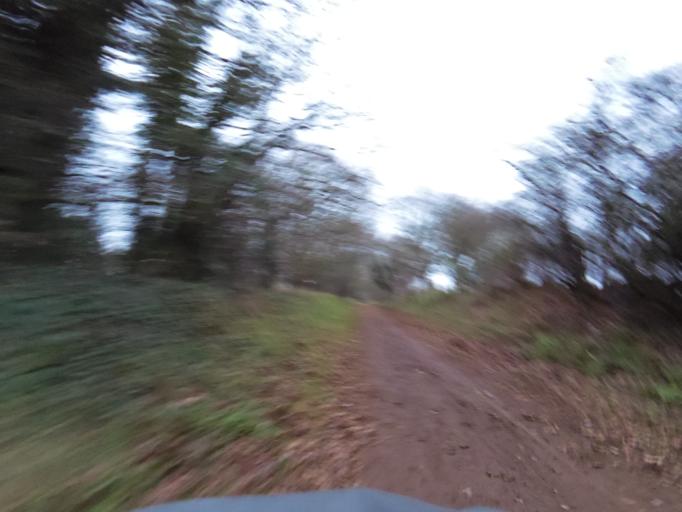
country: GB
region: England
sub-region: Norfolk
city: Horsford
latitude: 52.6975
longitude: 1.2015
